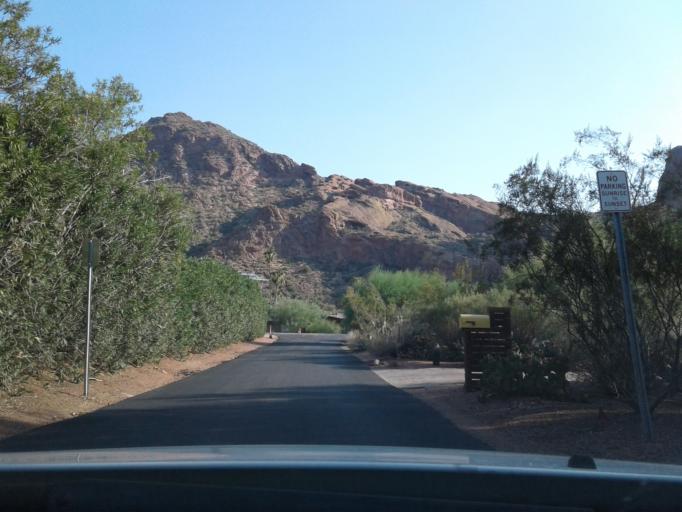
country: US
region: Arizona
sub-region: Maricopa County
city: Paradise Valley
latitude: 33.5245
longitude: -111.9649
